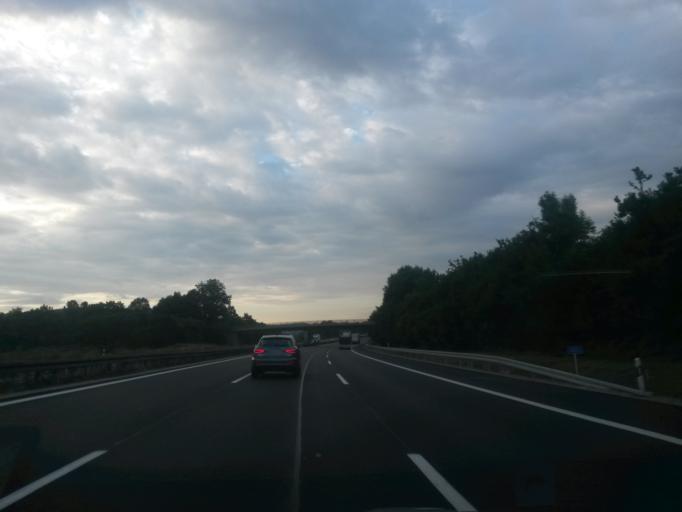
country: DE
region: Bavaria
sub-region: Regierungsbezirk Mittelfranken
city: Greding
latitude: 49.0629
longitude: 11.3200
